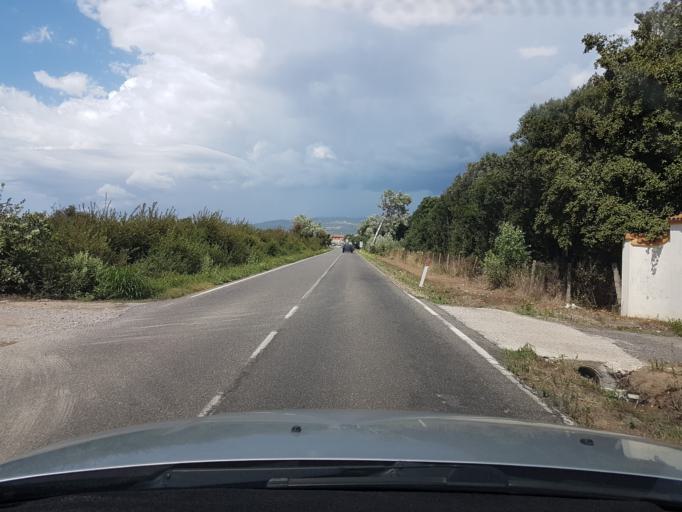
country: IT
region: Sardinia
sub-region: Provincia di Oristano
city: Riola Sardo
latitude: 39.9856
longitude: 8.5401
